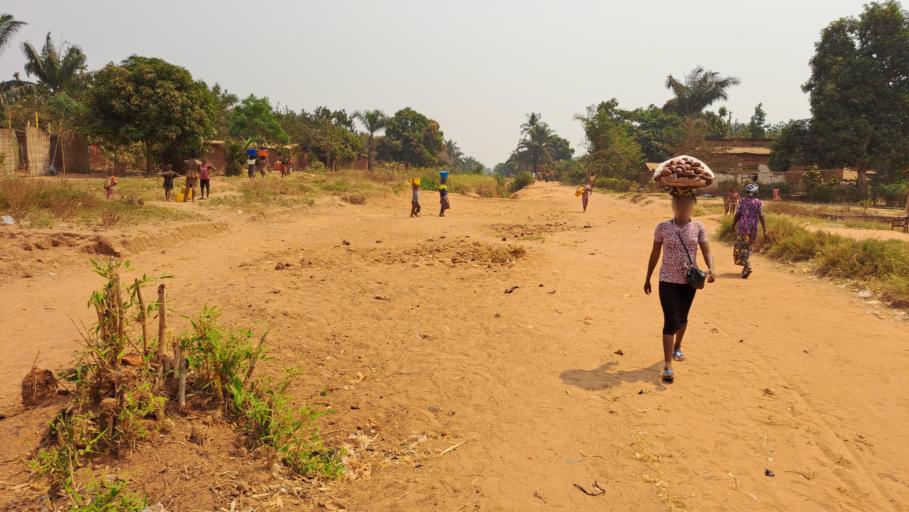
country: CD
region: Kasai-Oriental
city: Mbuji-Mayi
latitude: -6.0990
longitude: 23.5677
